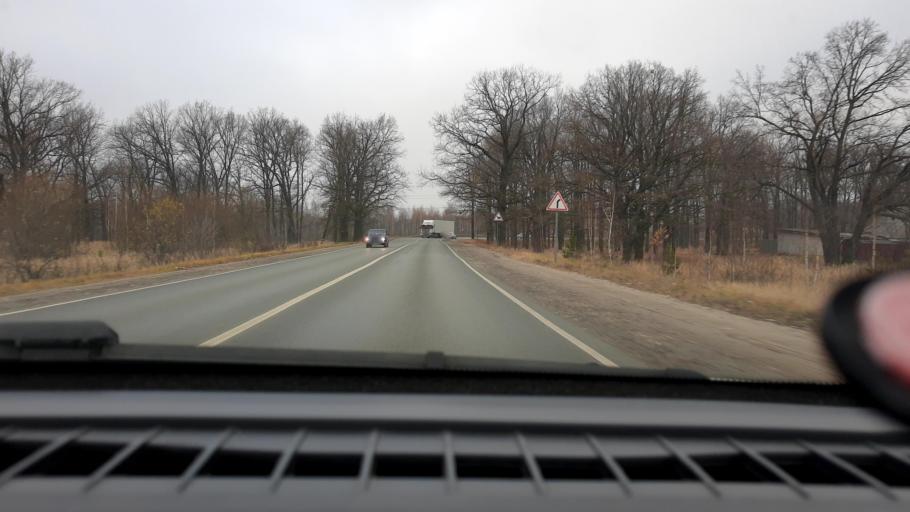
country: RU
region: Nizjnij Novgorod
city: Novaya Balakhna
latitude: 56.5126
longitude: 43.5789
